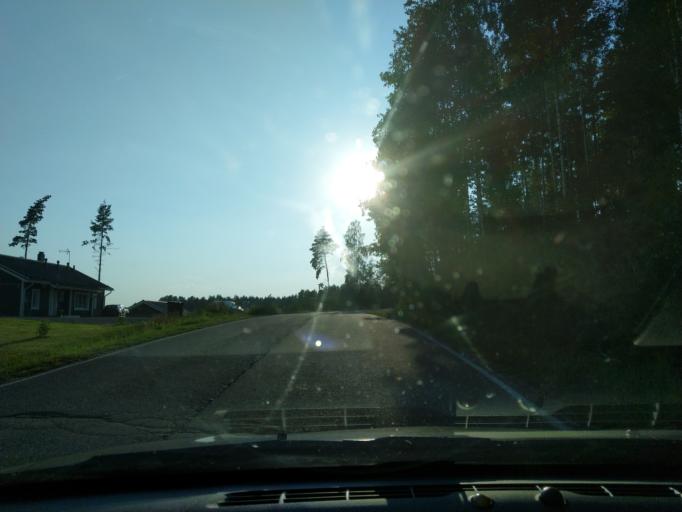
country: FI
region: Uusimaa
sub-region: Helsinki
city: Vihti
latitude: 60.5333
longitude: 24.3454
